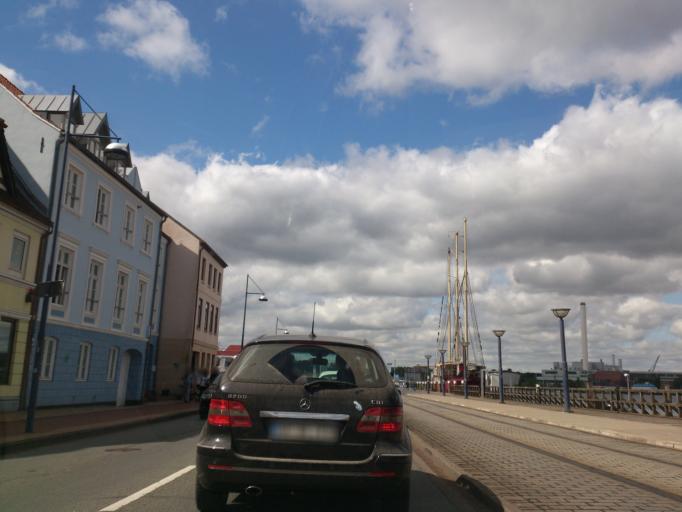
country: DE
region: Schleswig-Holstein
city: Flensburg
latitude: 54.7945
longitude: 9.4329
